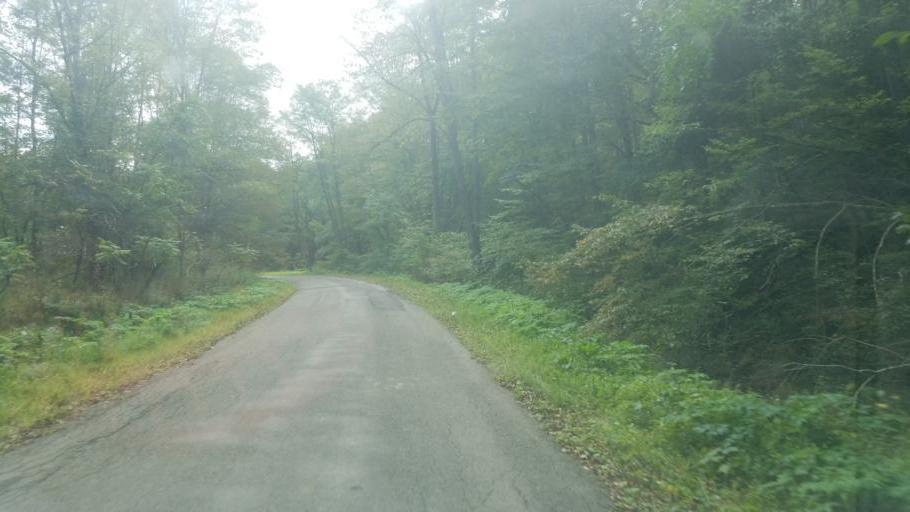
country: US
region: New York
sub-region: Allegany County
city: Cuba
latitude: 42.2193
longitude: -78.3361
